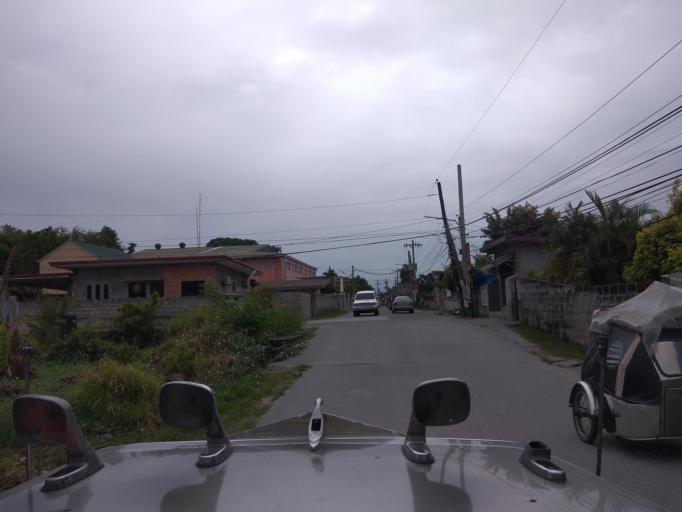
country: PH
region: Central Luzon
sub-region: Province of Pampanga
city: Mexico
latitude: 15.0619
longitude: 120.7177
